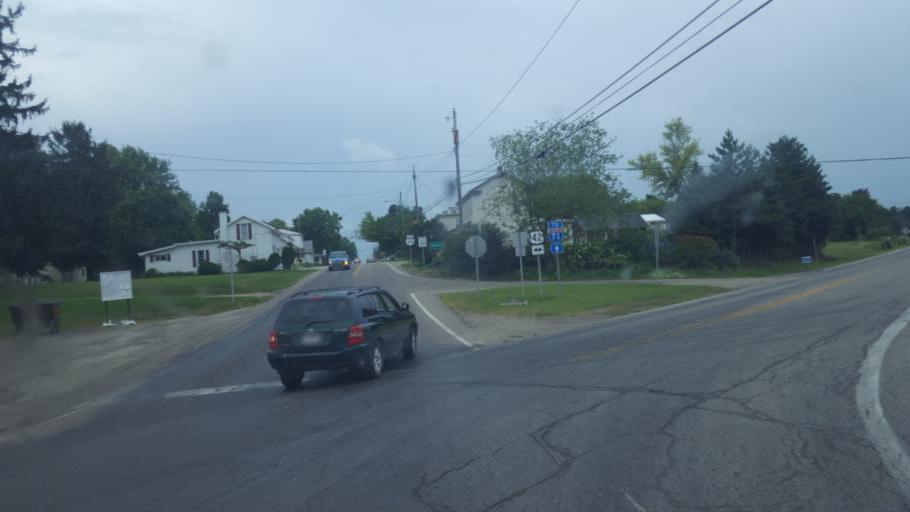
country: US
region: Ohio
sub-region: Richland County
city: Lexington
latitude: 40.6233
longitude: -82.6632
